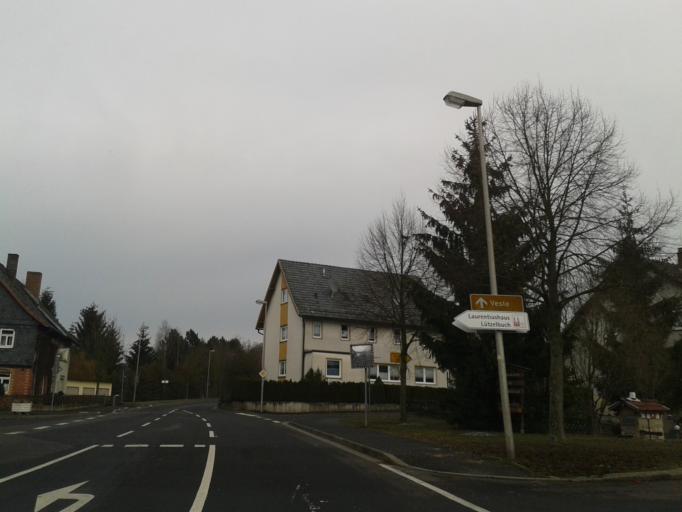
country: DE
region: Bavaria
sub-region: Upper Franconia
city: Niederfullbach
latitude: 50.2549
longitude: 11.0135
